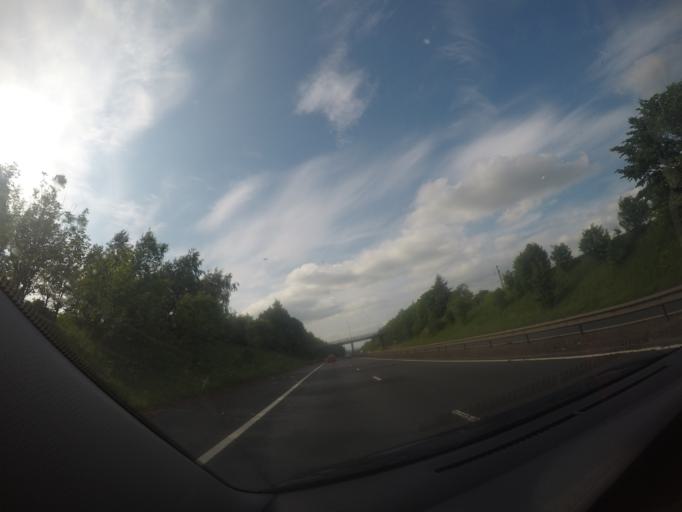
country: GB
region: Scotland
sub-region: South Lanarkshire
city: Lesmahagow
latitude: 55.6363
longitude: -3.8724
